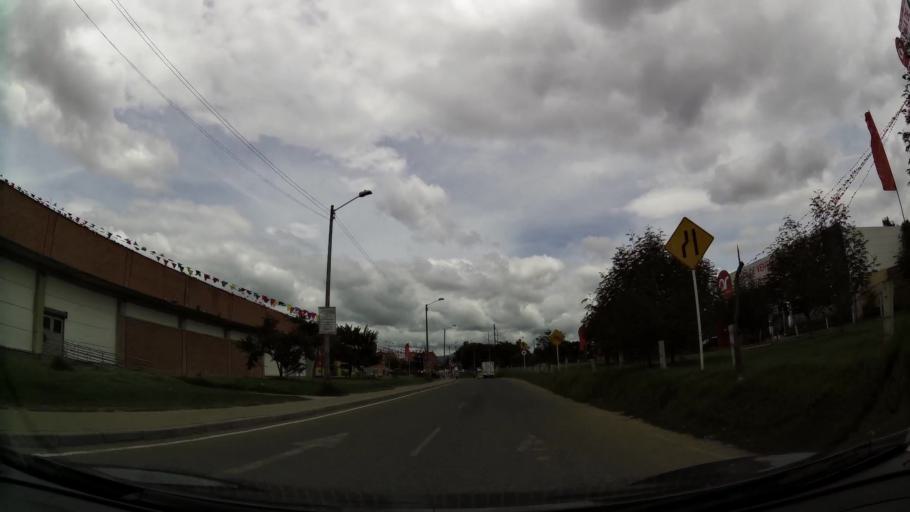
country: CO
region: Cundinamarca
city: Funza
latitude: 4.7203
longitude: -74.1230
